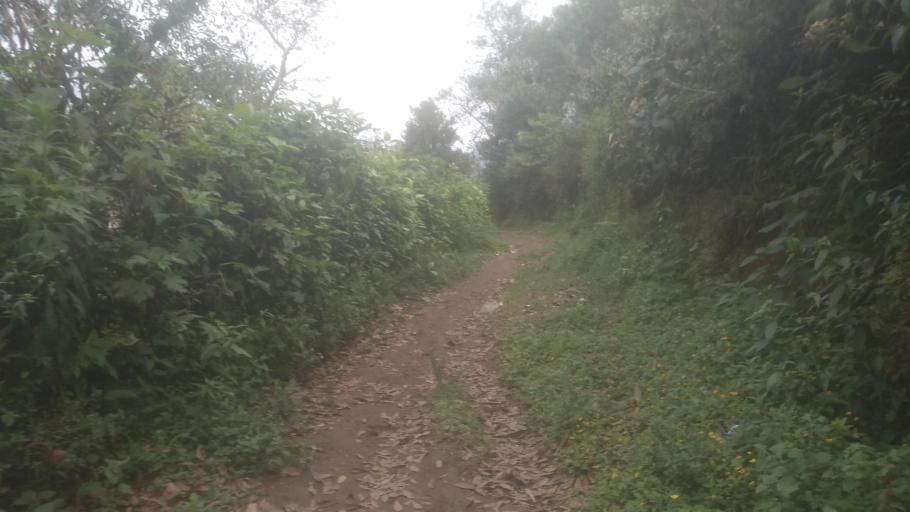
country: MX
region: Veracruz
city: Chocaman
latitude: 18.9917
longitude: -97.0532
